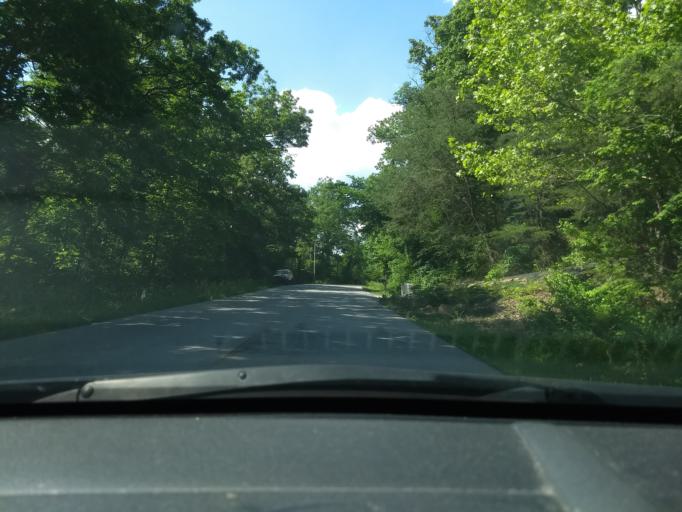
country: US
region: Indiana
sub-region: Floyd County
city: New Albany
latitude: 38.2608
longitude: -85.8619
